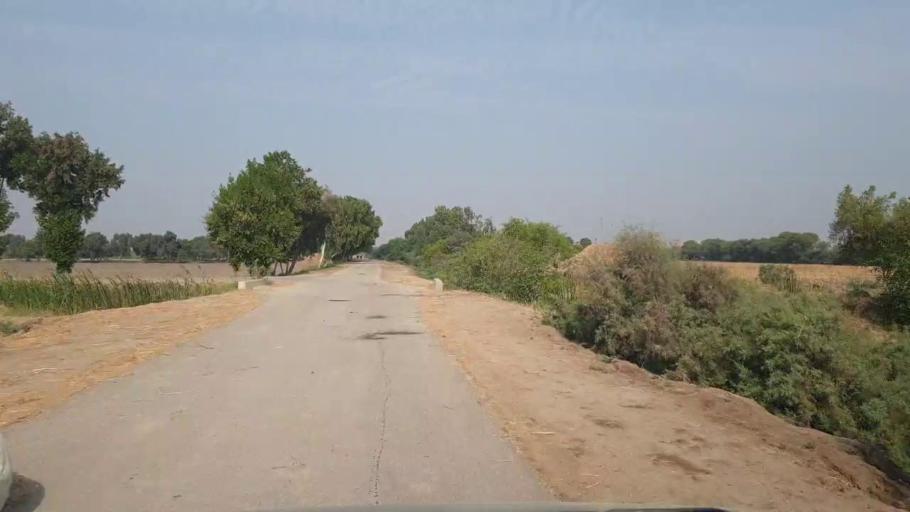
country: PK
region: Sindh
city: Tando Muhammad Khan
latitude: 25.1224
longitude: 68.4591
